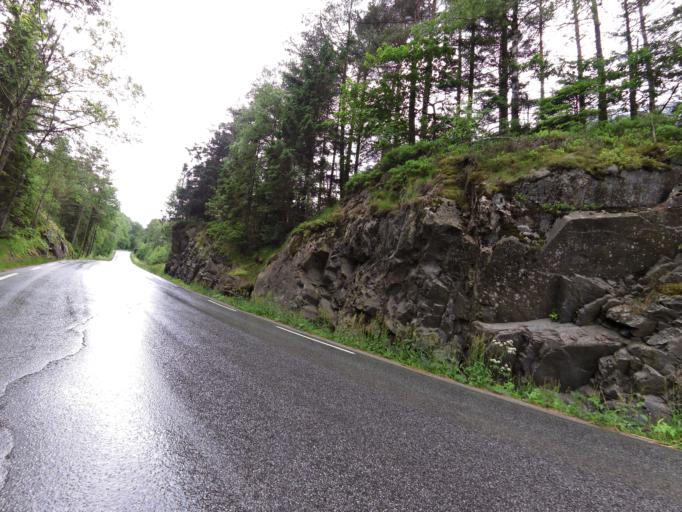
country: NO
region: Vest-Agder
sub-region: Mandal
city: Mandal
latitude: 58.0258
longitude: 7.5171
